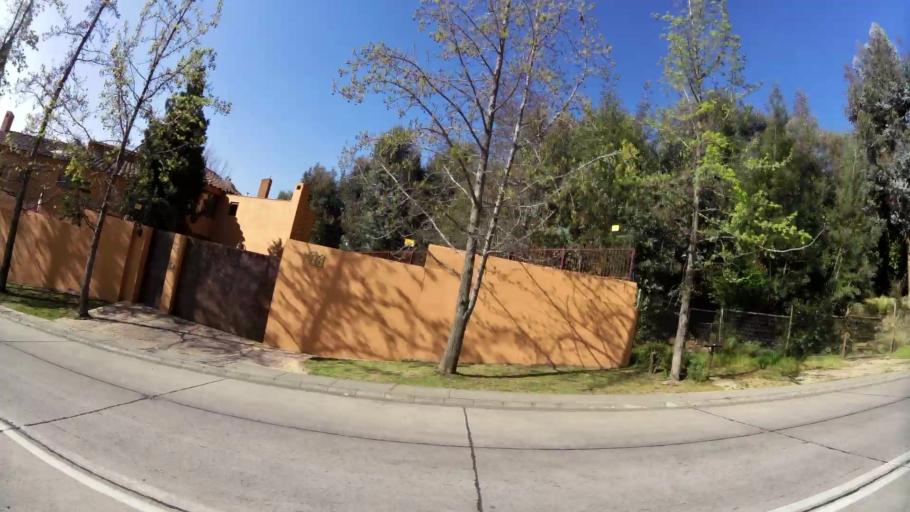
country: CL
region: Santiago Metropolitan
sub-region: Provincia de Santiago
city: Villa Presidente Frei, Nunoa, Santiago, Chile
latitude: -33.3700
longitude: -70.4978
